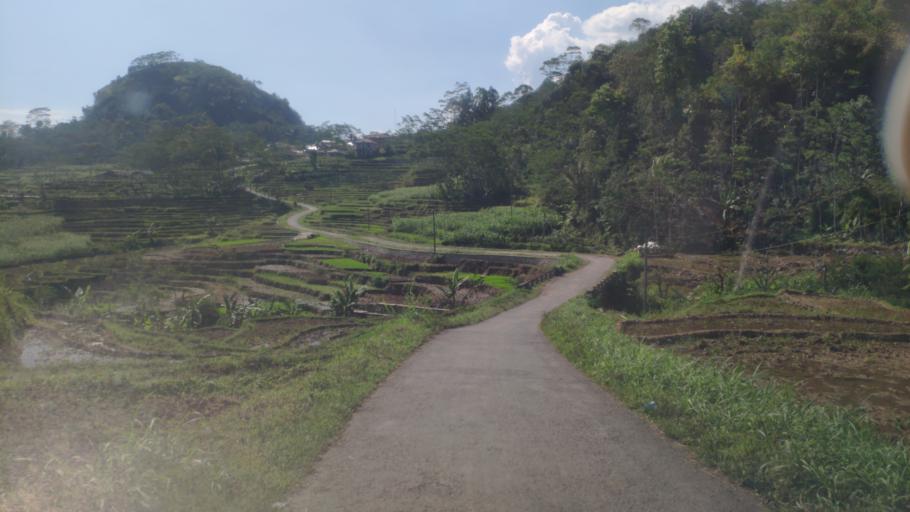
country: ID
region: Central Java
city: Buaran
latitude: -7.2272
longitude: 109.6043
